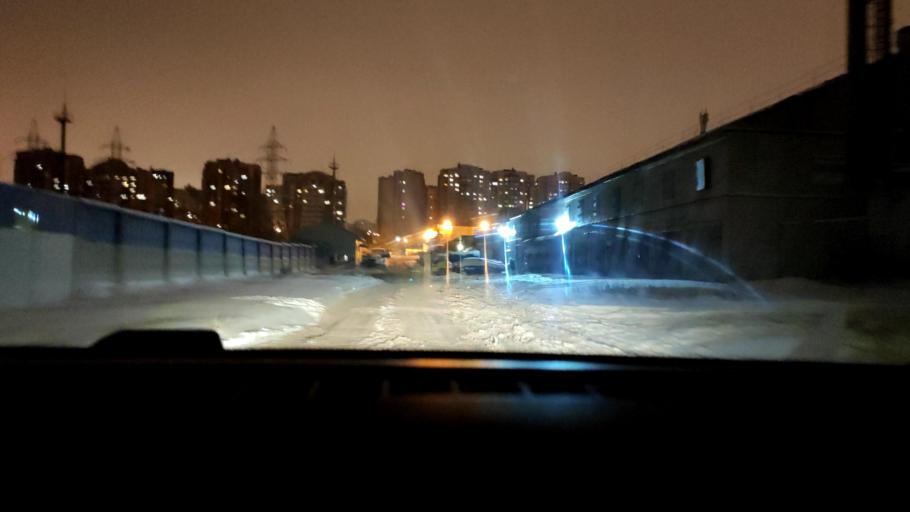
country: RU
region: Samara
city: Samara
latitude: 53.2470
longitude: 50.1823
